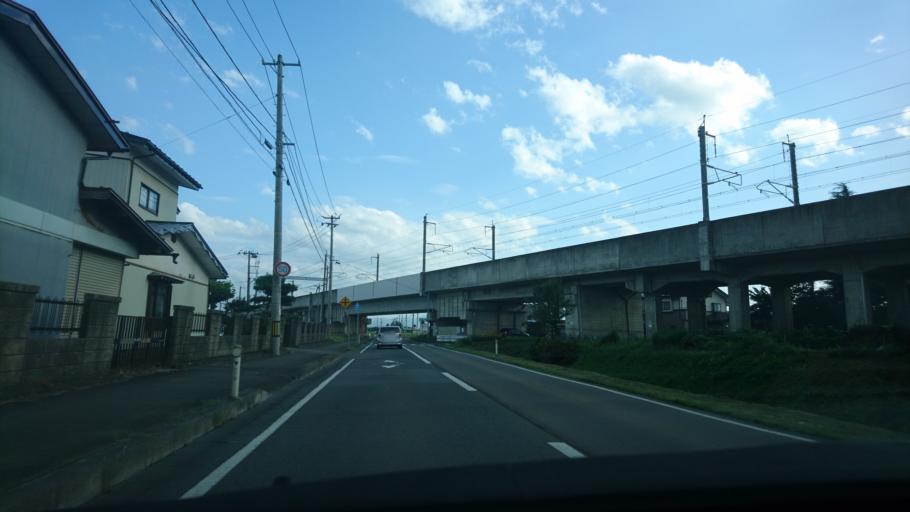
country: JP
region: Iwate
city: Mizusawa
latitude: 39.1738
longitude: 141.1776
